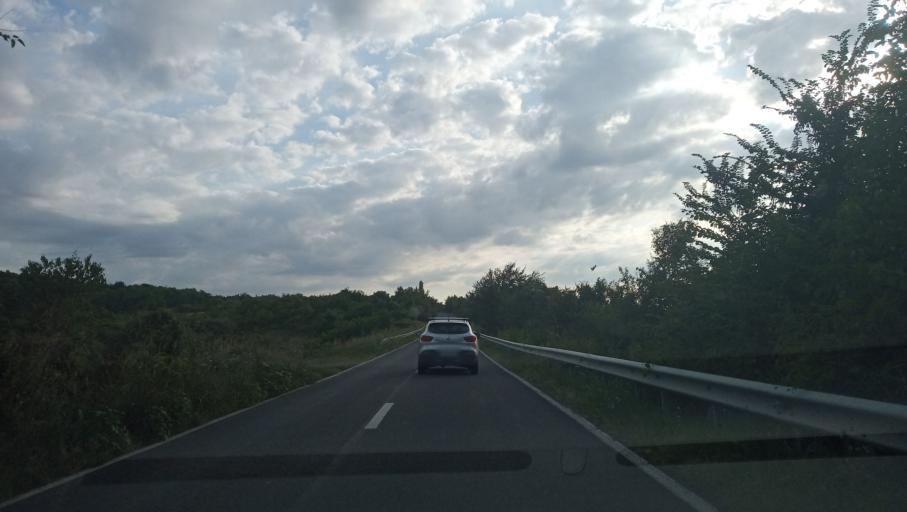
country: RO
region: Constanta
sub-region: Comuna Ostrov
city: Ostrov
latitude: 44.1127
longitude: 27.3209
